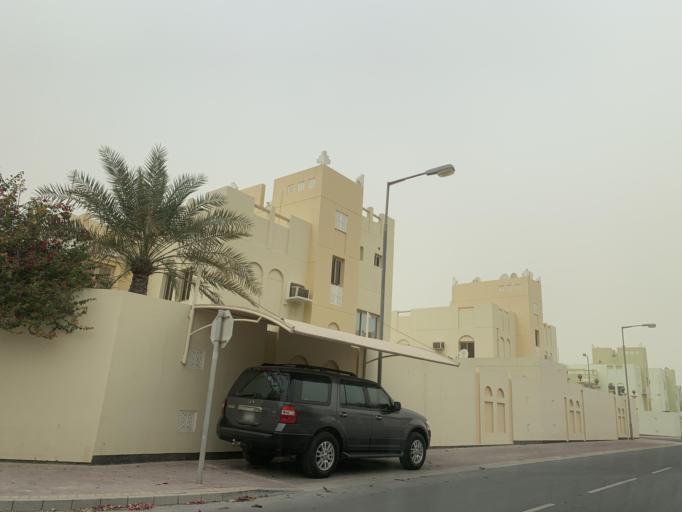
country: BH
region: Central Governorate
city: Madinat Hamad
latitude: 26.1259
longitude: 50.5099
